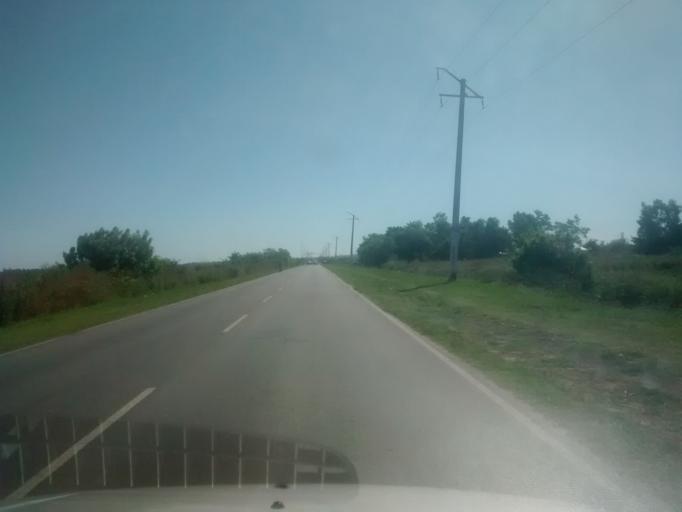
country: AR
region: Buenos Aires
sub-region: Partido de Berisso
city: Berisso
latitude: -34.8897
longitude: -57.8682
